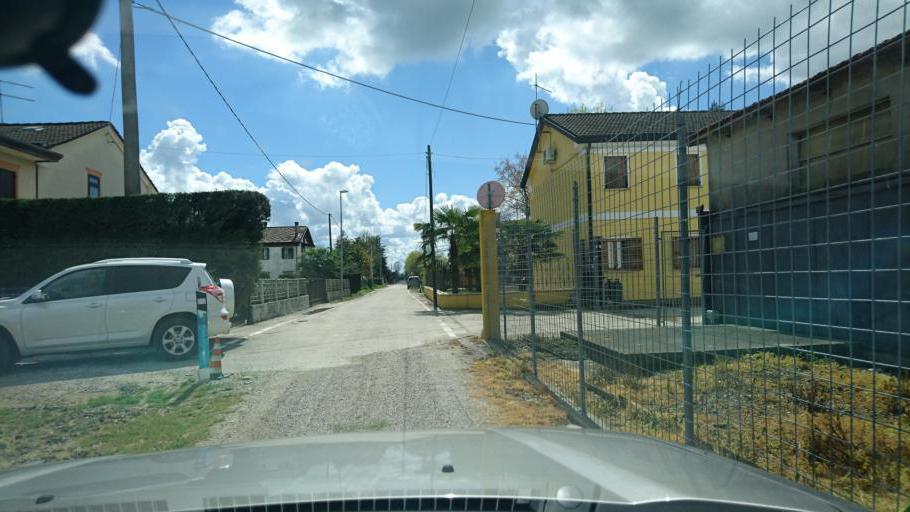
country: IT
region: Veneto
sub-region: Provincia di Padova
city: Piazzola sul Brenta
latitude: 45.5444
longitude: 11.7668
